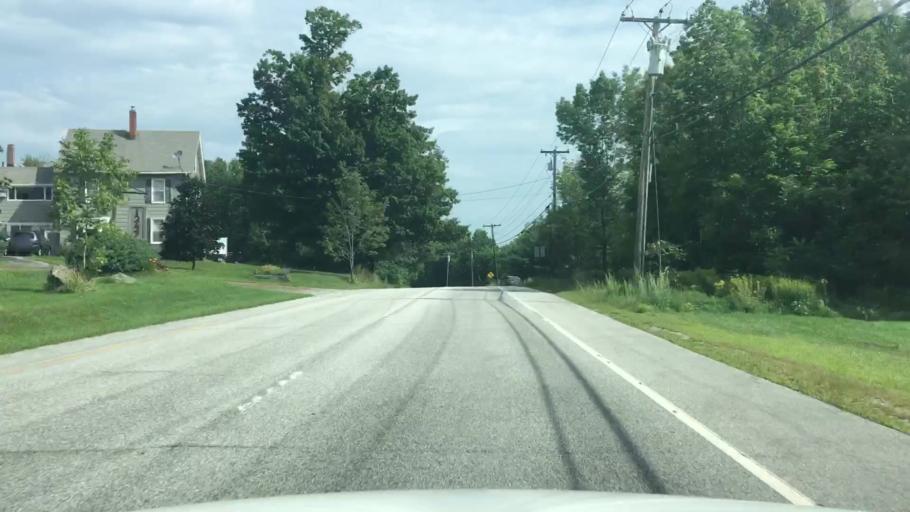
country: US
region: Maine
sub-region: Androscoggin County
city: Auburn
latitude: 44.0507
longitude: -70.2545
